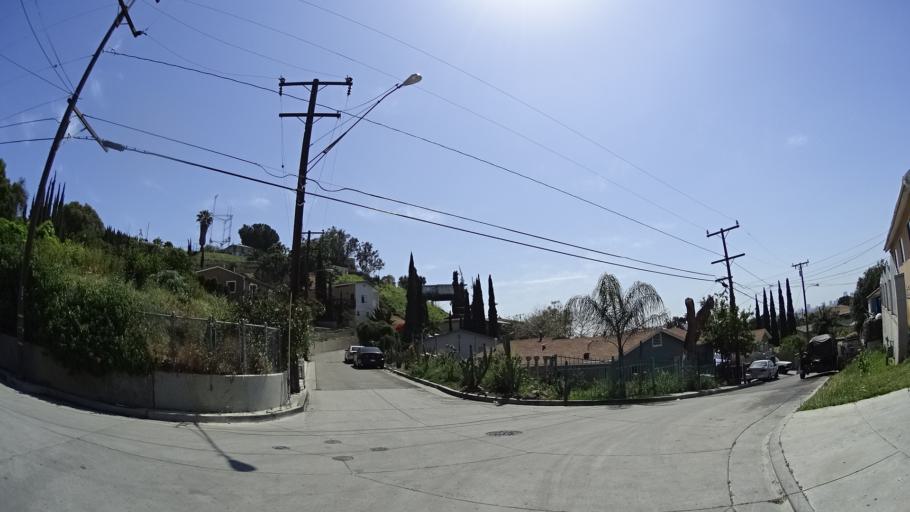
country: US
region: California
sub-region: Los Angeles County
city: Boyle Heights
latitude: 34.0537
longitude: -118.1910
